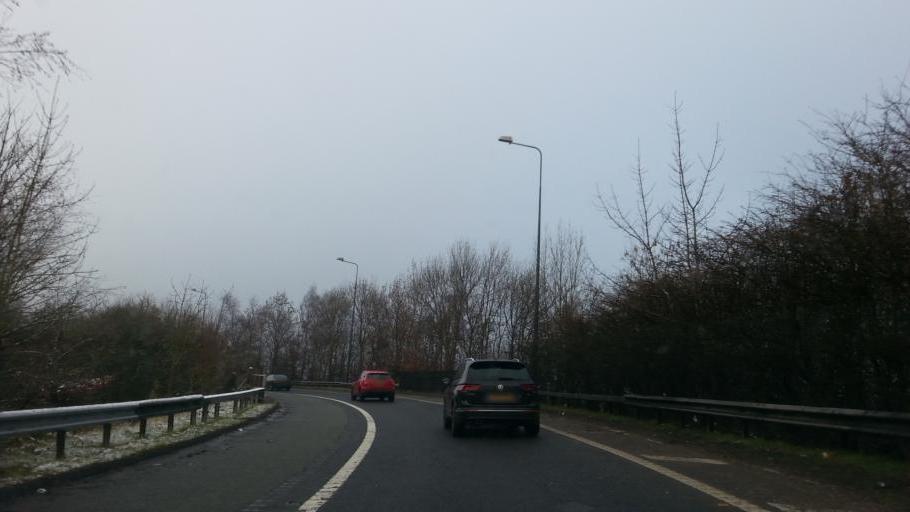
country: GB
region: England
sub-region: Manchester
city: Didsbury
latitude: 53.3977
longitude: -2.2275
